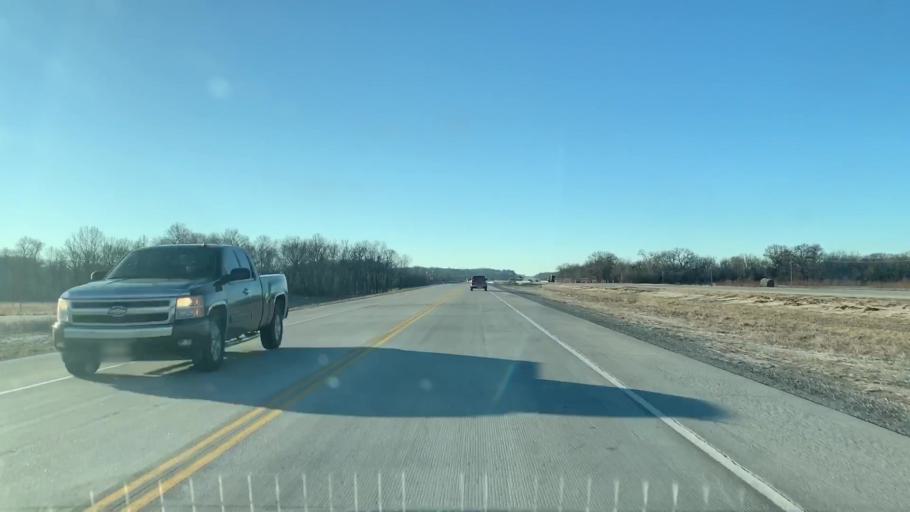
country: US
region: Kansas
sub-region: Crawford County
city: Arma
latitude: 37.6844
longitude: -94.7036
